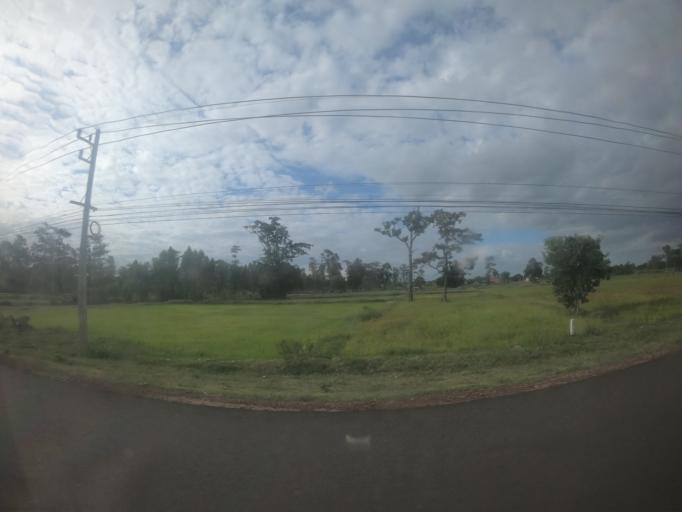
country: TH
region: Surin
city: Prasat
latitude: 14.5895
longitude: 103.4660
